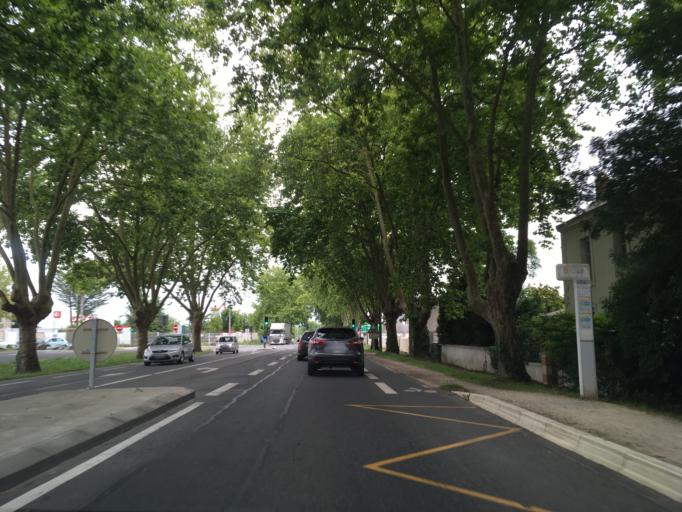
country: FR
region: Poitou-Charentes
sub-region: Departement des Deux-Sevres
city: Bessines
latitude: 46.3076
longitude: -0.4851
